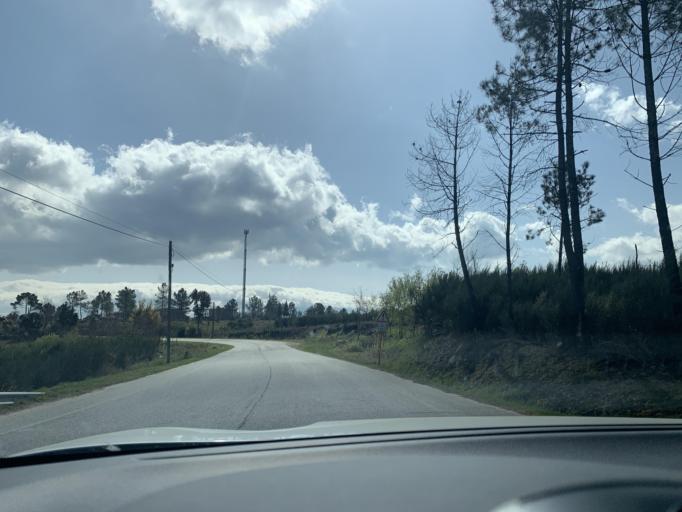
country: PT
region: Guarda
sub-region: Fornos de Algodres
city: Fornos de Algodres
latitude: 40.6147
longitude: -7.6095
